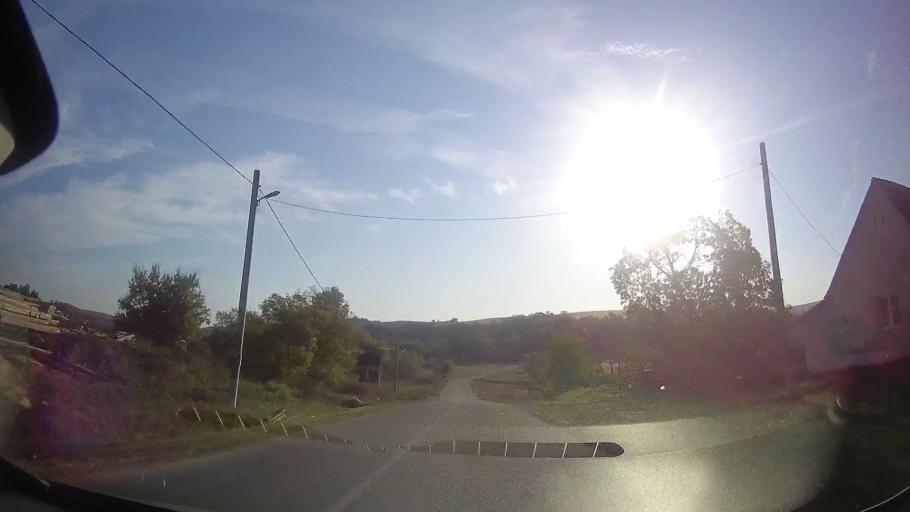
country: RO
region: Timis
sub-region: Comuna Bogda
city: Bogda
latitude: 45.9739
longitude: 21.5984
